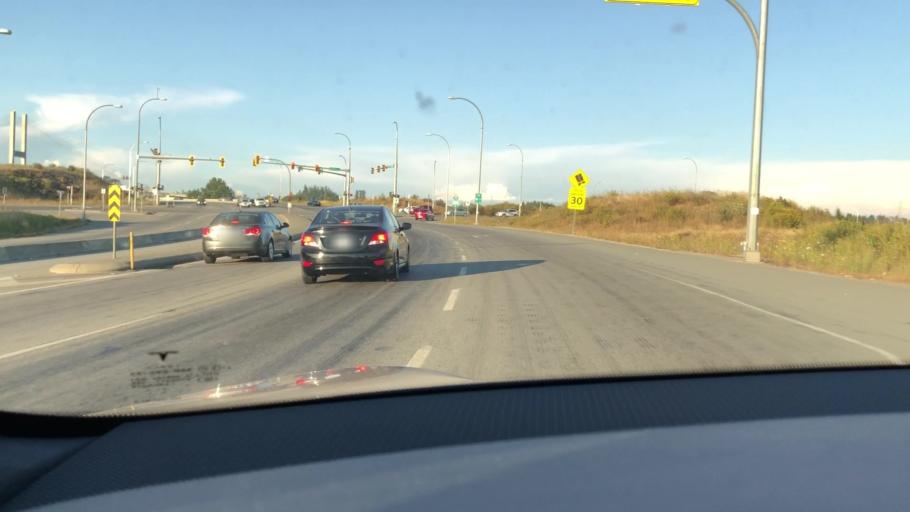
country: CA
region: British Columbia
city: Delta
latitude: 49.1481
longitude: -122.9549
